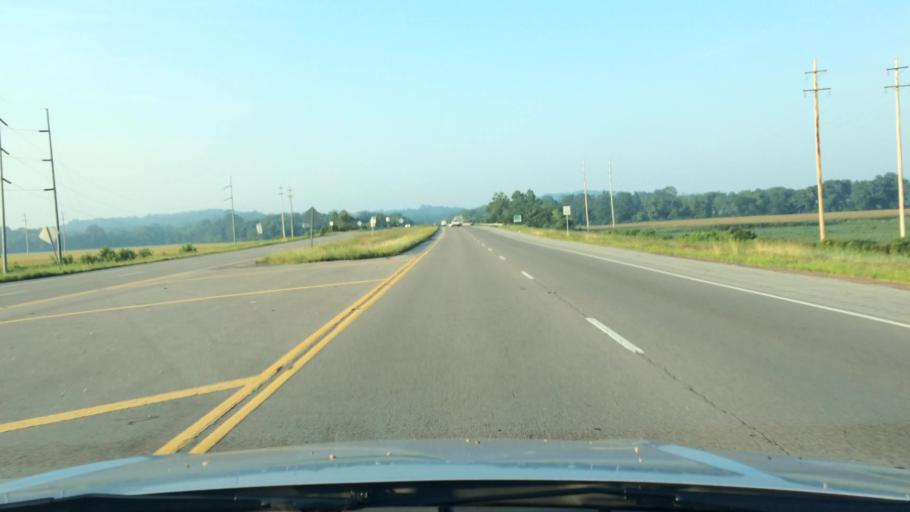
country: US
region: Tennessee
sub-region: Giles County
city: Pulaski
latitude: 35.2027
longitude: -87.0632
